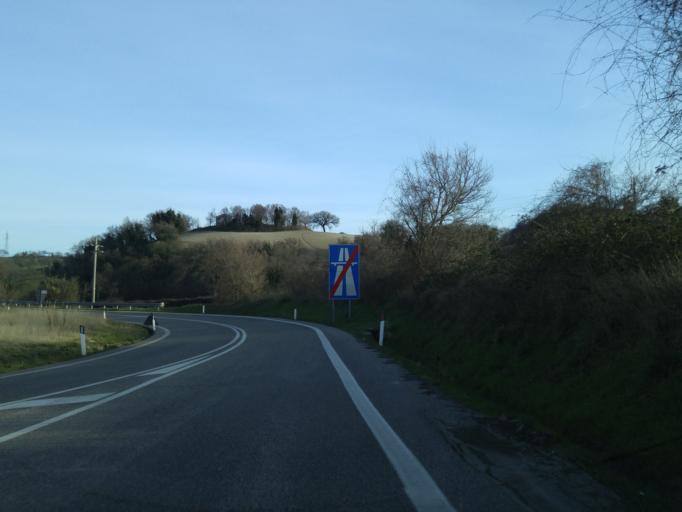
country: IT
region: The Marches
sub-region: Provincia di Pesaro e Urbino
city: Fossombrone
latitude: 43.6871
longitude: 12.8337
